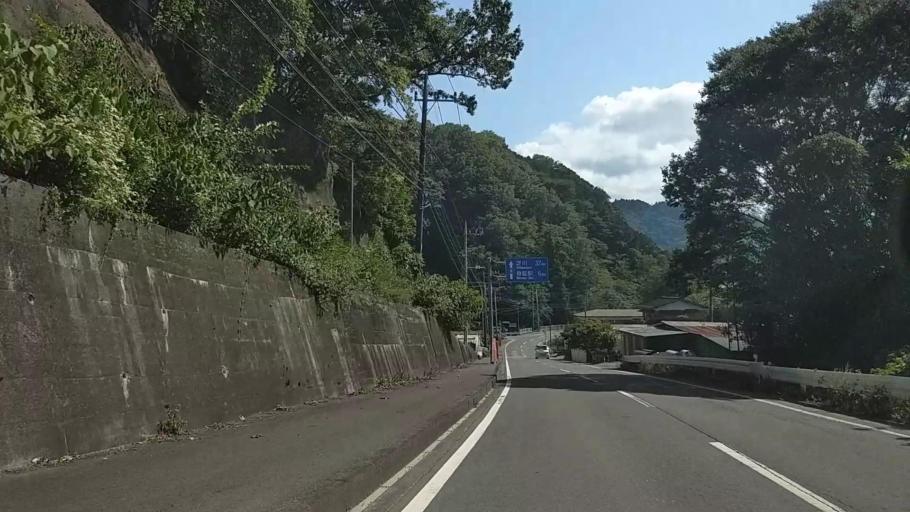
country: JP
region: Yamanashi
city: Ryuo
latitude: 35.4121
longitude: 138.4568
